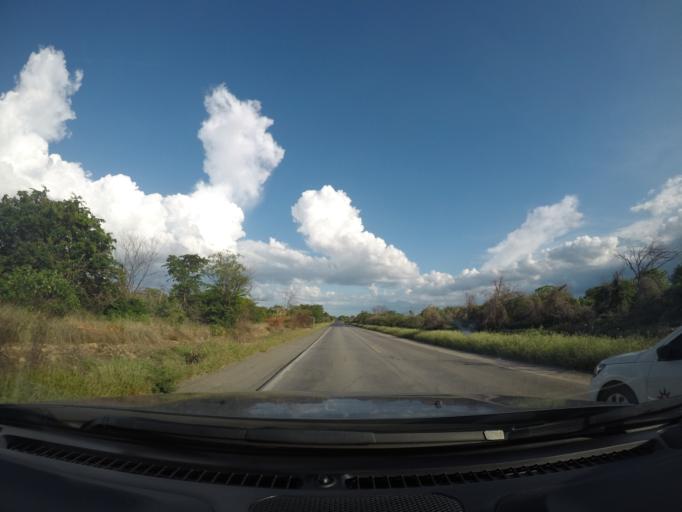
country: BR
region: Bahia
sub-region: Oliveira Dos Brejinhos
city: Oliveira dos Brejinhos
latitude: -12.0854
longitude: -42.9378
